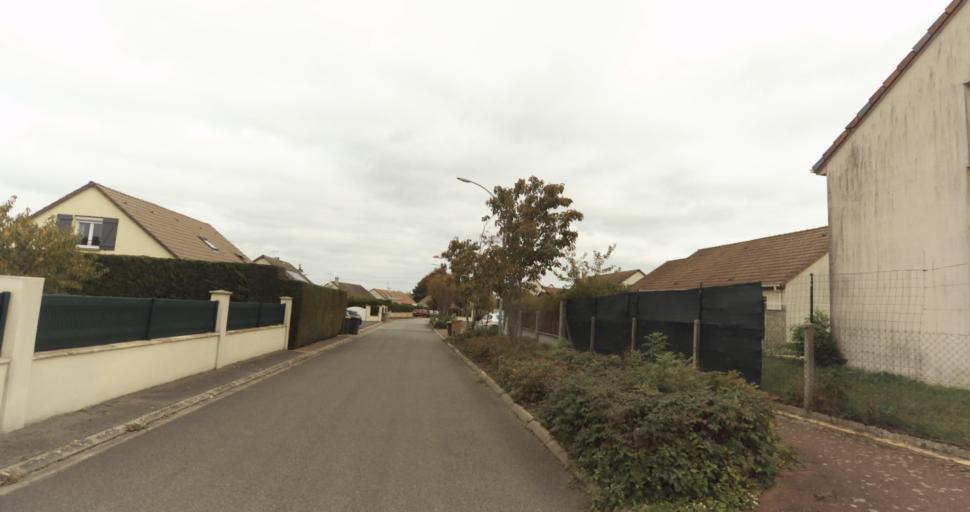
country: FR
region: Centre
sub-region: Departement d'Eure-et-Loir
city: Vernouillet
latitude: 48.7174
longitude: 1.3590
